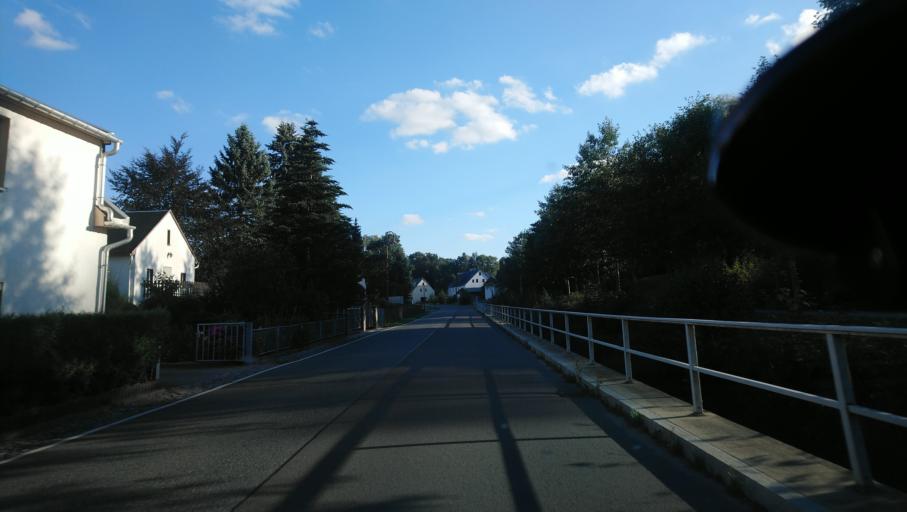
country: DE
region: Saxony
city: Crottendorf
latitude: 50.5240
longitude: 12.9439
